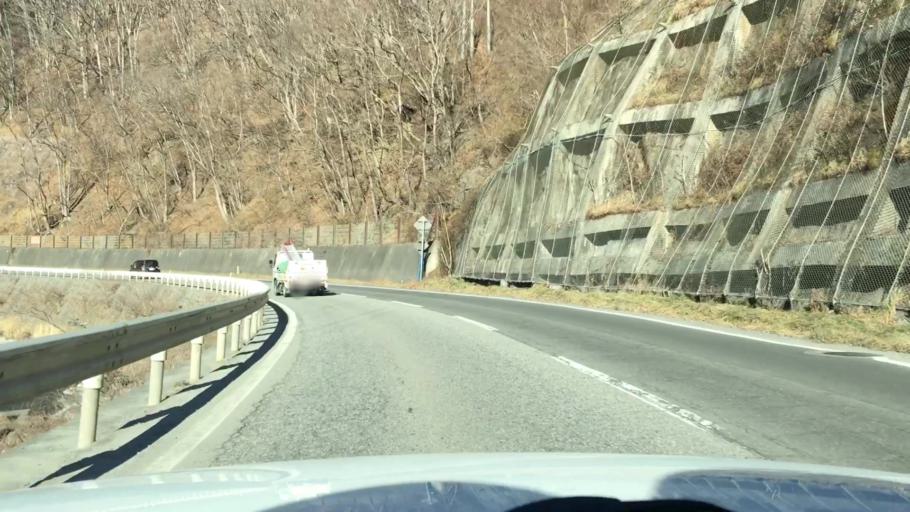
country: JP
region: Iwate
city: Miyako
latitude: 39.6256
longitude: 141.8239
